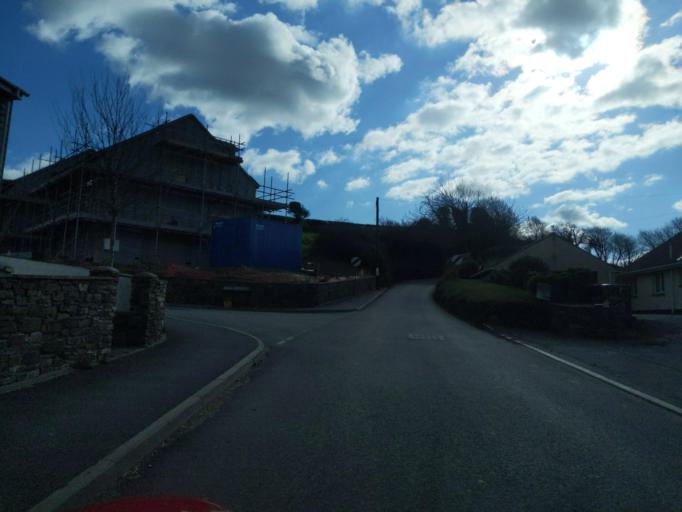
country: GB
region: England
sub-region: Devon
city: Salcombe
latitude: 50.2694
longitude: -3.7204
